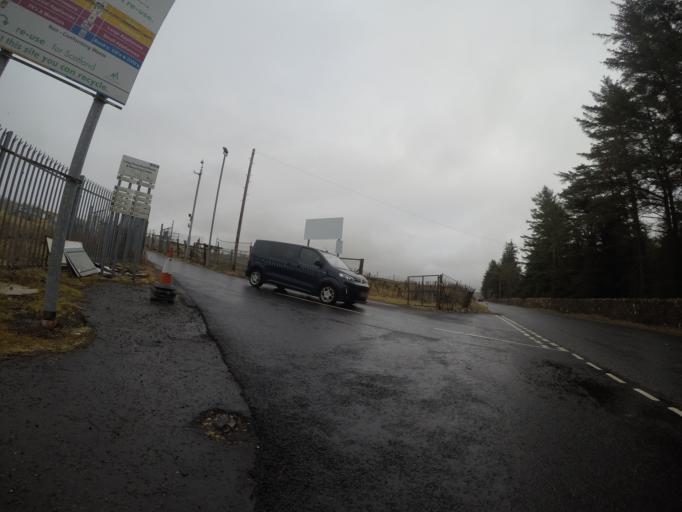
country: GB
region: Scotland
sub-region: North Ayrshire
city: Fairlie
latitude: 55.7759
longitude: -4.8244
